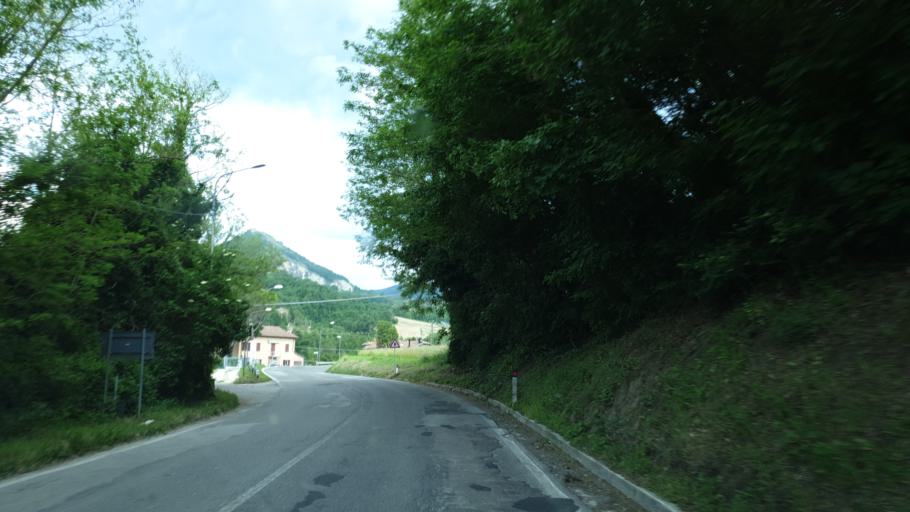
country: IT
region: Emilia-Romagna
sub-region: Provincia di Rimini
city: Talamello
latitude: 43.9038
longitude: 12.2938
